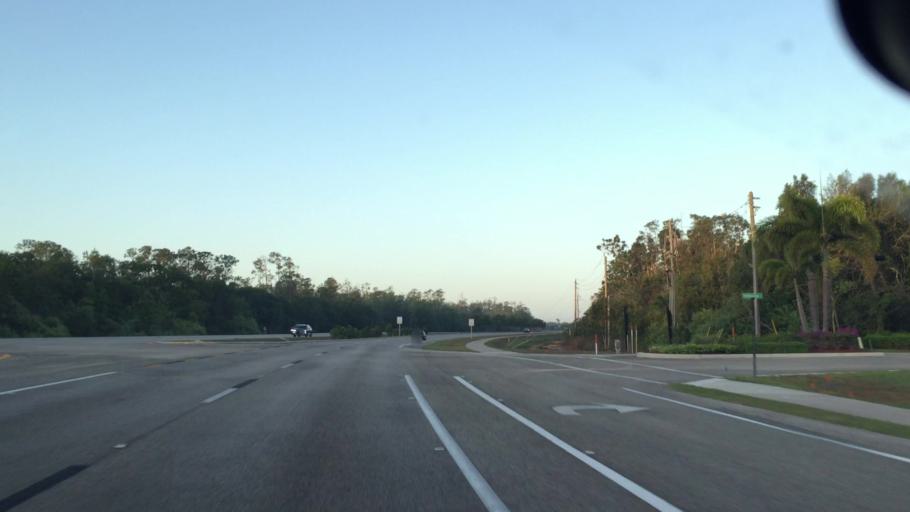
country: US
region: Florida
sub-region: Lee County
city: Villas
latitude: 26.5580
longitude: -81.8332
